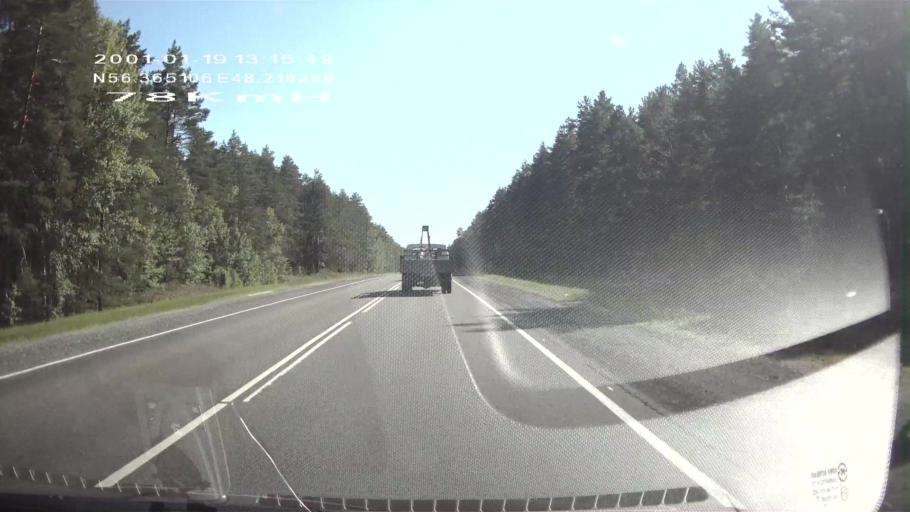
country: RU
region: Mariy-El
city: Suslonger
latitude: 56.3649
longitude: 48.2144
